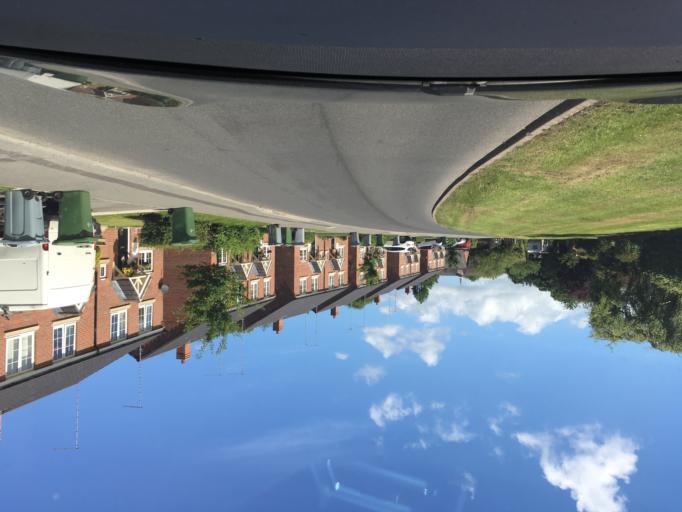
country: GB
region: England
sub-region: Cheshire East
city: Mobberley
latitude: 53.2882
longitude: -2.3339
